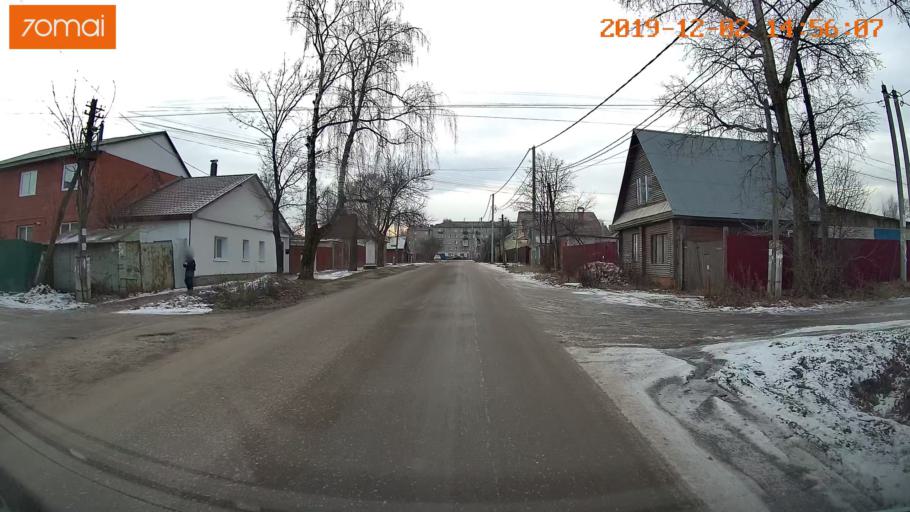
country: RU
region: Ivanovo
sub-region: Gorod Ivanovo
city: Ivanovo
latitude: 56.9718
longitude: 41.0169
